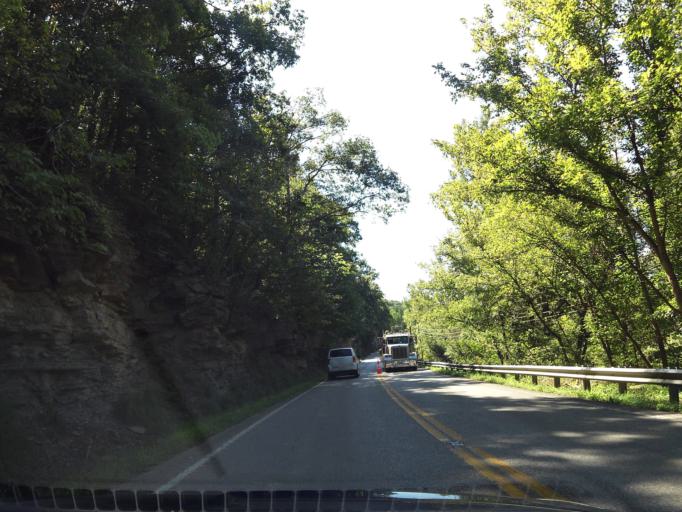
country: US
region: Kentucky
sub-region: Clay County
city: Manchester
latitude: 37.0886
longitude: -83.6910
